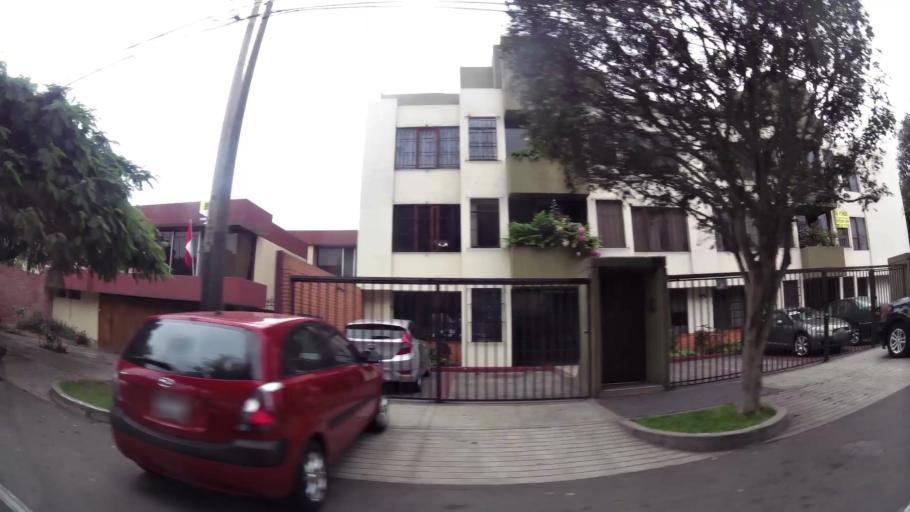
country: PE
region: Lima
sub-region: Lima
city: San Luis
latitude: -12.1014
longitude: -77.0119
